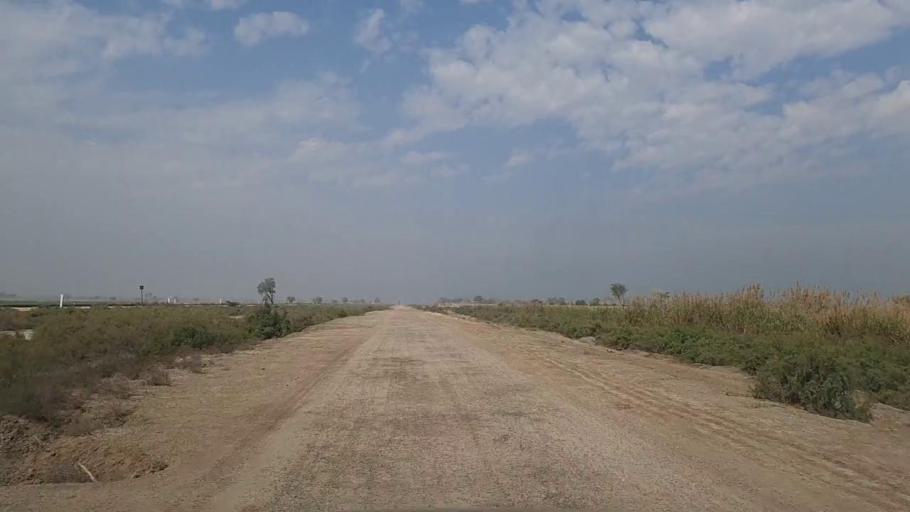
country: PK
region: Sindh
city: Daur
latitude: 26.3888
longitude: 68.3511
